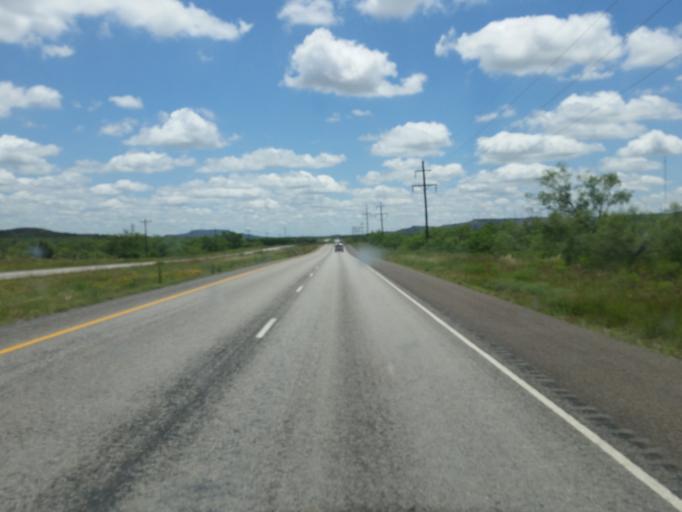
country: US
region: Texas
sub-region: Garza County
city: Post
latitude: 33.0000
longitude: -101.1583
